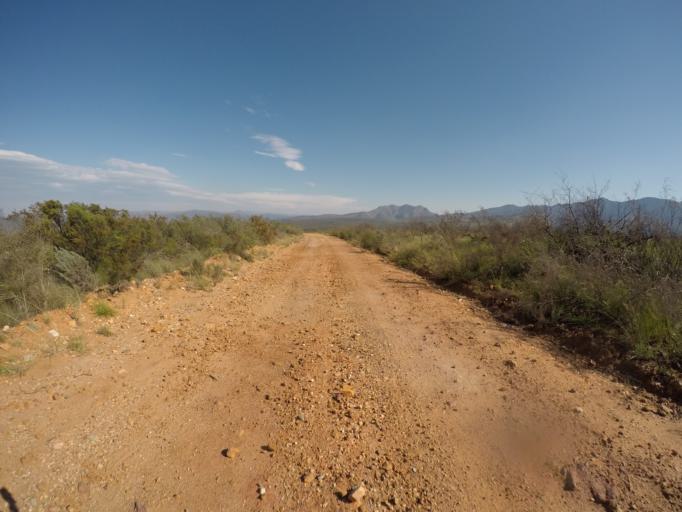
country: ZA
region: Eastern Cape
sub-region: Cacadu District Municipality
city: Kareedouw
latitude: -33.6354
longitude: 24.4649
